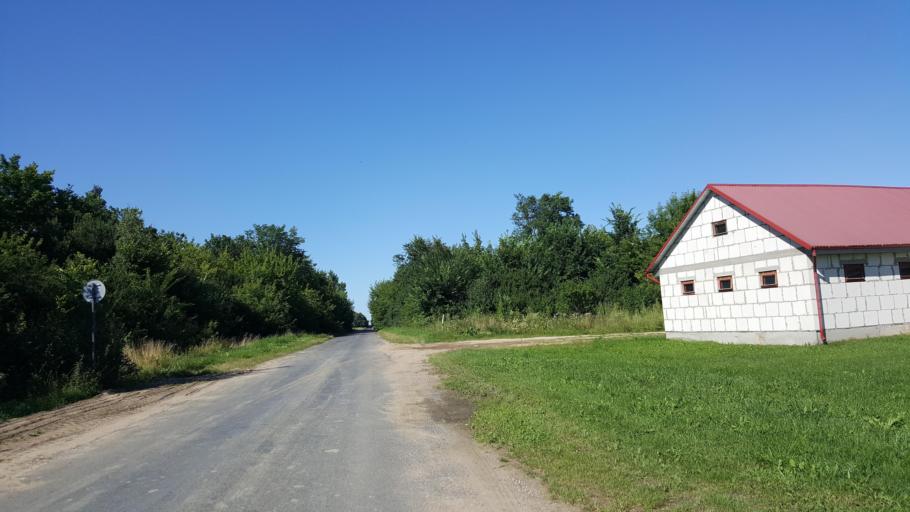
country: BY
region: Brest
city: Charnawchytsy
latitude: 52.2278
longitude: 23.7402
